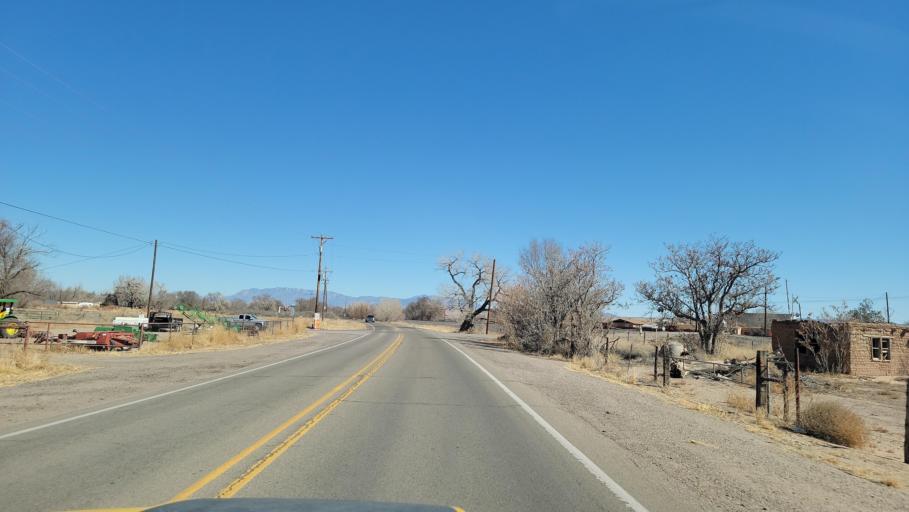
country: US
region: New Mexico
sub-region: Valencia County
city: Bosque Farms
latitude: 34.9099
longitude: -106.6974
